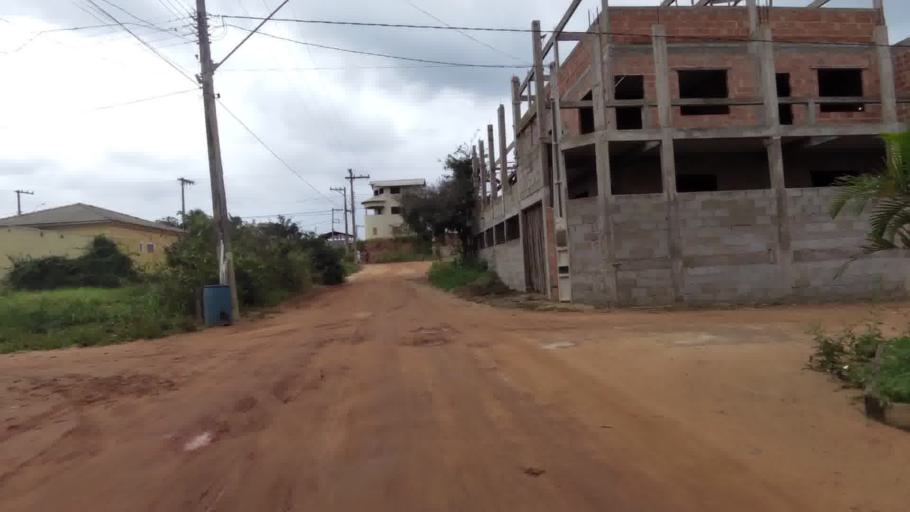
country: BR
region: Espirito Santo
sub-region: Marataizes
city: Marataizes
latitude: -21.0678
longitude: -40.8379
